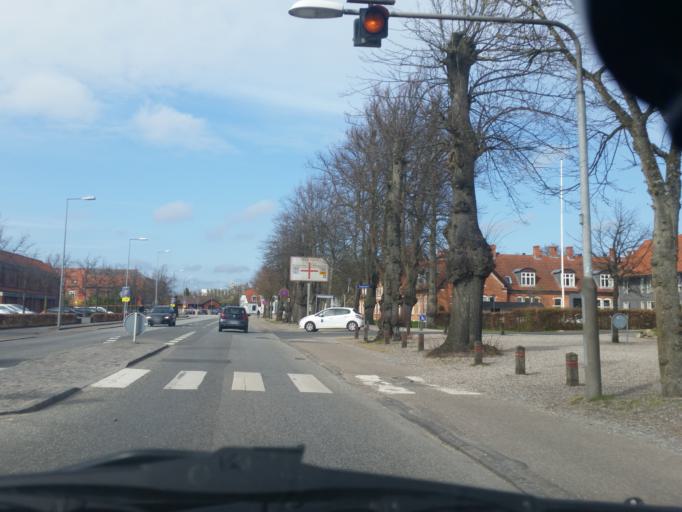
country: DK
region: Zealand
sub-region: Soro Kommune
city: Soro
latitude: 55.4371
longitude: 11.5592
